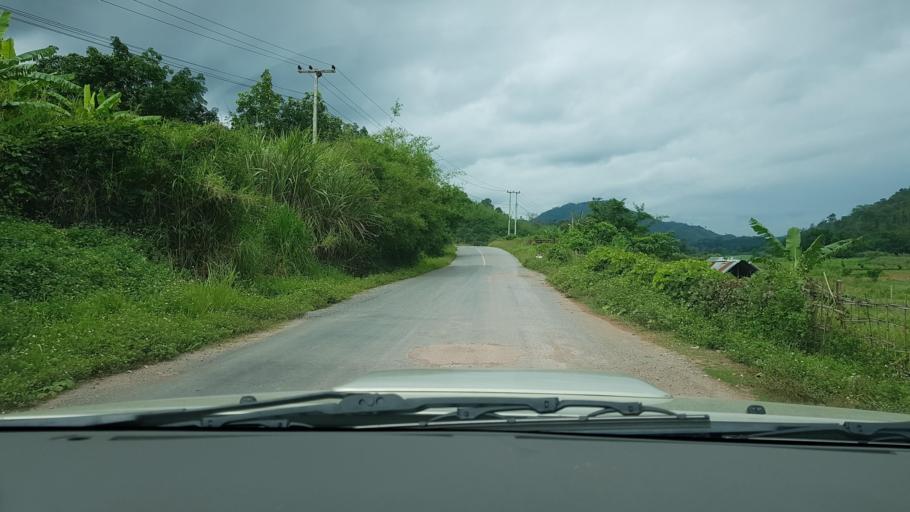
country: LA
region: Loungnamtha
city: Muang Nale
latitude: 20.3989
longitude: 101.7555
